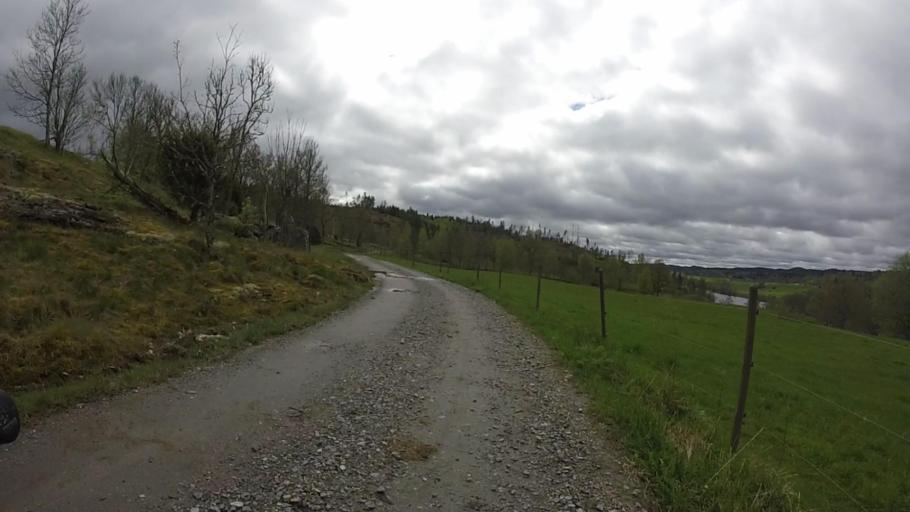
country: SE
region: Vaestra Goetaland
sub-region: Trollhattan
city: Sjuntorp
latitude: 58.2423
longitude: 12.2071
